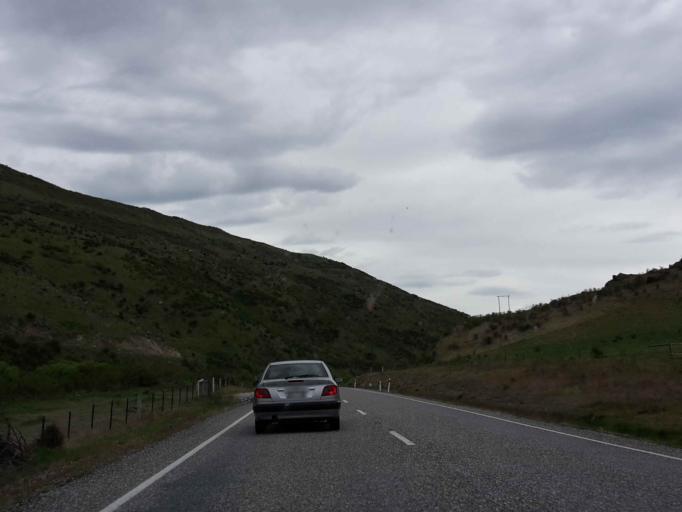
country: NZ
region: Otago
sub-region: Queenstown-Lakes District
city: Wanaka
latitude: -44.7314
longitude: 169.5083
